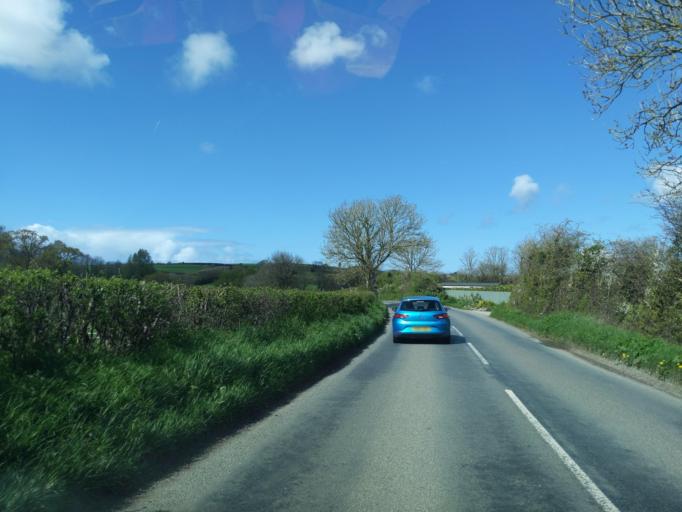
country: GB
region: England
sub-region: Cornwall
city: Wadebridge
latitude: 50.5402
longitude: -4.8555
